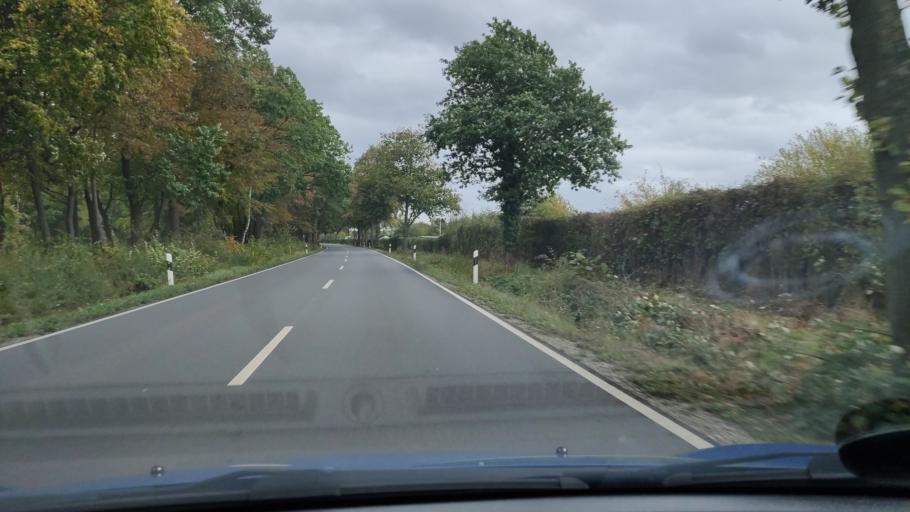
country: DE
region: Lower Saxony
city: Seelze
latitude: 52.3883
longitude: 9.6057
